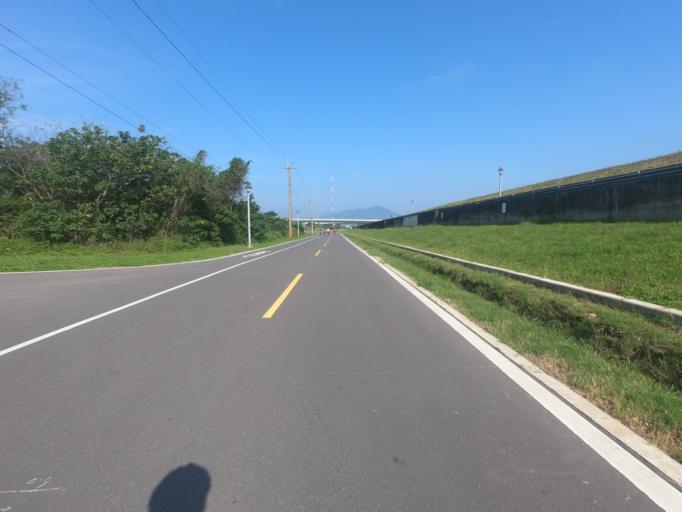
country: TW
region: Taipei
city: Taipei
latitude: 25.0976
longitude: 121.5032
